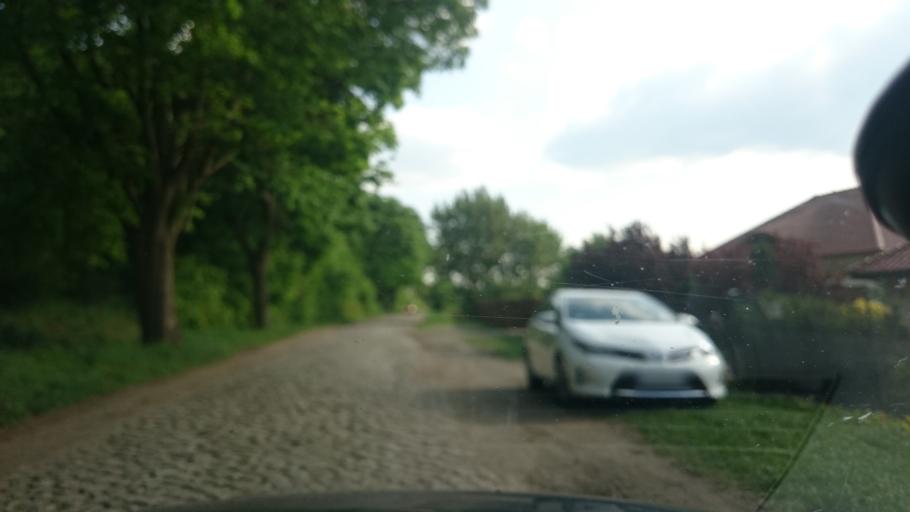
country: PL
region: Kujawsko-Pomorskie
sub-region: Grudziadz
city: Grudziadz
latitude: 53.4840
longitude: 18.8131
